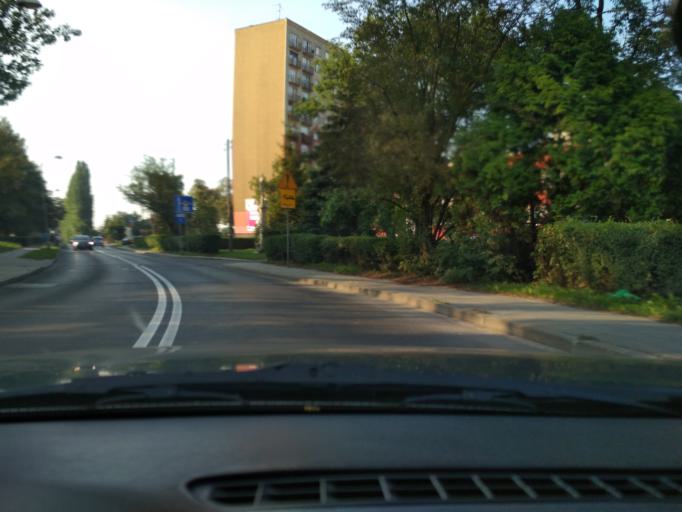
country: PL
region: Silesian Voivodeship
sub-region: Gliwice
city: Gliwice
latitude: 50.2837
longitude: 18.6752
